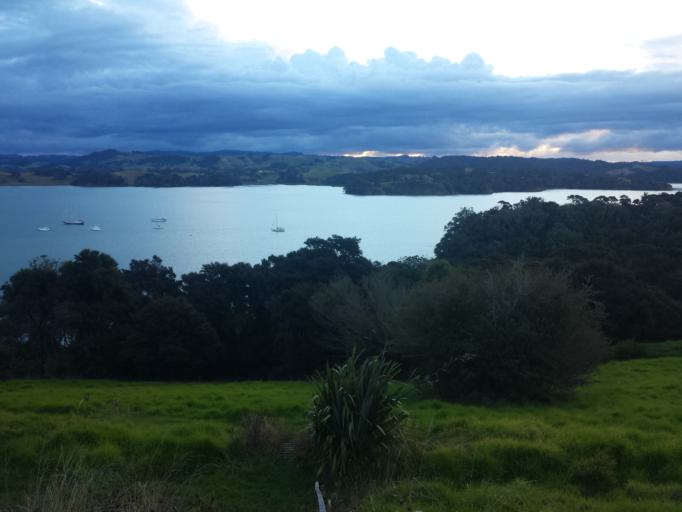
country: NZ
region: Auckland
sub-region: Auckland
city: Warkworth
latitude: -36.4752
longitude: 174.7327
